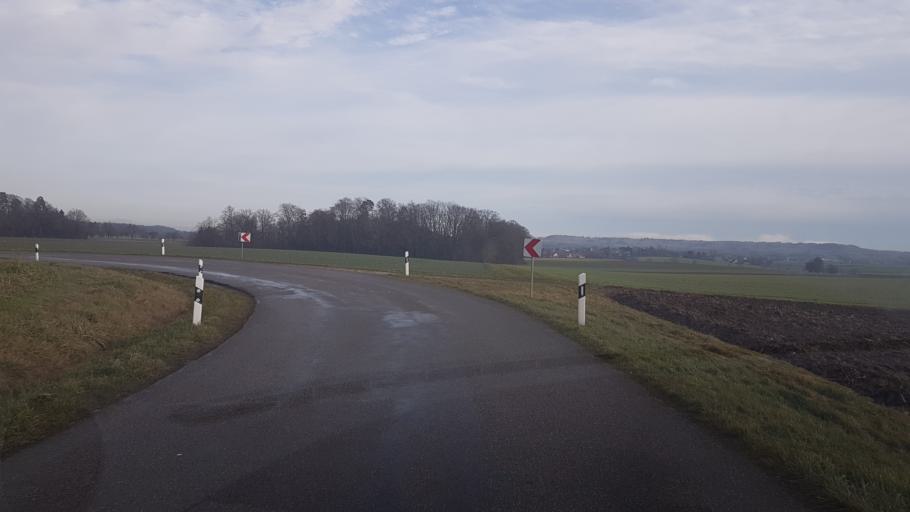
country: DE
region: Baden-Wuerttemberg
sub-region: Regierungsbezirk Stuttgart
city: Wallhausen
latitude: 49.2332
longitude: 10.0927
